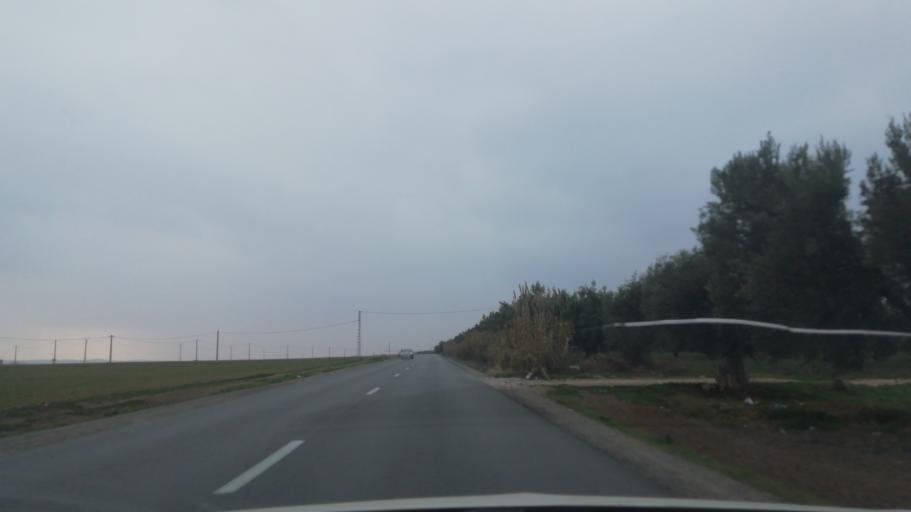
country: DZ
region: Sidi Bel Abbes
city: Sfizef
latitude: 35.2507
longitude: -0.2018
